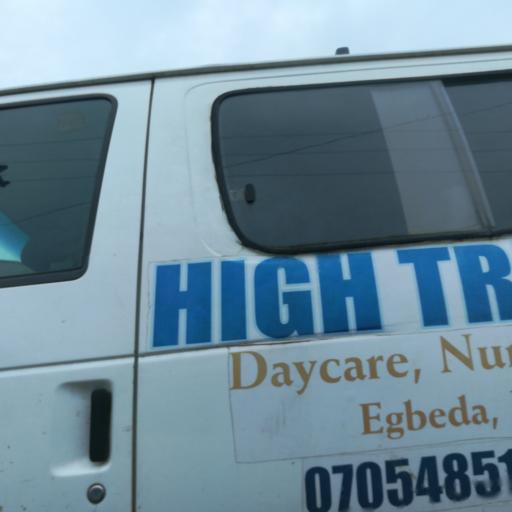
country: NG
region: Lagos
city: Makoko
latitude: 6.5026
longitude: 3.3807
